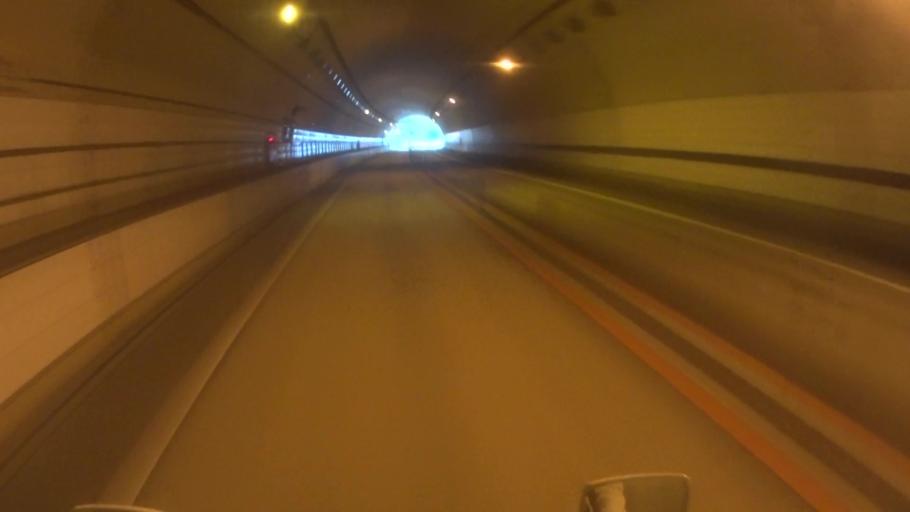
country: JP
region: Kyoto
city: Miyazu
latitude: 35.4743
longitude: 135.1753
